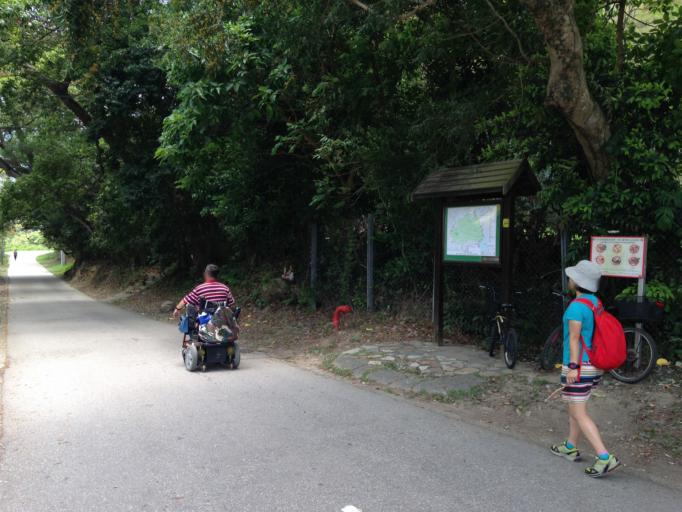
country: CN
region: Guangdong
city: Haishan
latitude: 22.5245
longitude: 114.2083
